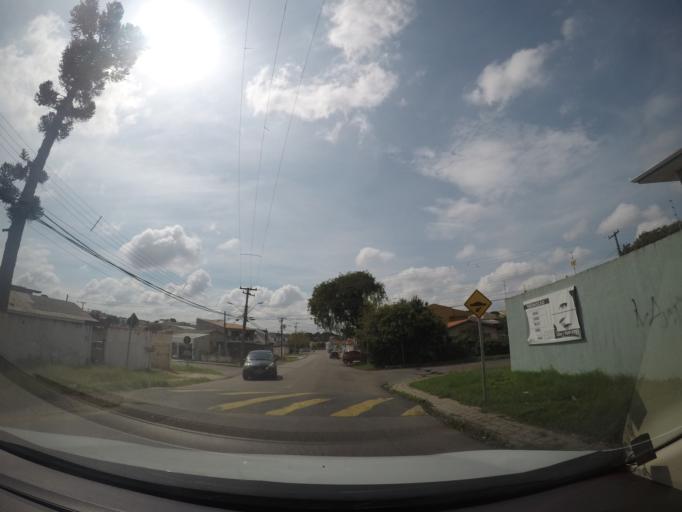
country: BR
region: Parana
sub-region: Curitiba
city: Curitiba
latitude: -25.4887
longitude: -49.2849
